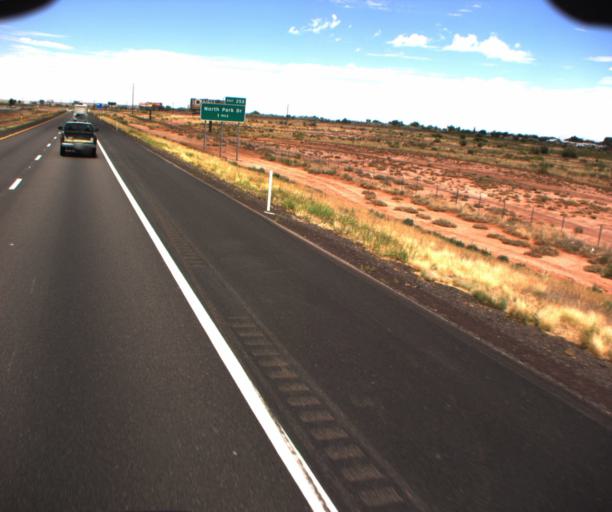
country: US
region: Arizona
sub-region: Navajo County
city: Winslow
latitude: 35.0274
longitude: -110.6830
